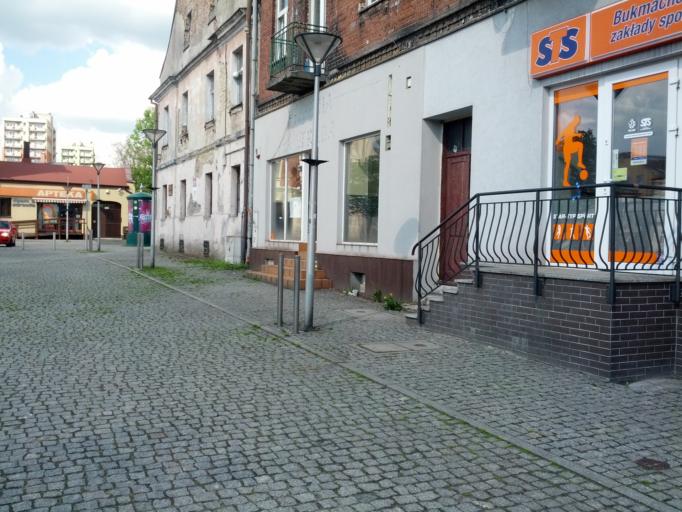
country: PL
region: Silesian Voivodeship
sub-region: Powiat bedzinski
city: Czeladz
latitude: 50.3182
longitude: 19.0740
